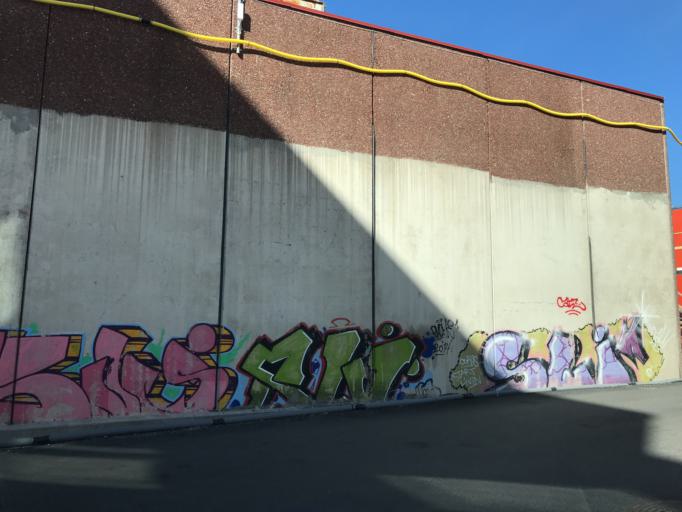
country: SE
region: Stockholm
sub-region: Sollentuna Kommun
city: Sollentuna
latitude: 59.4341
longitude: 17.9412
